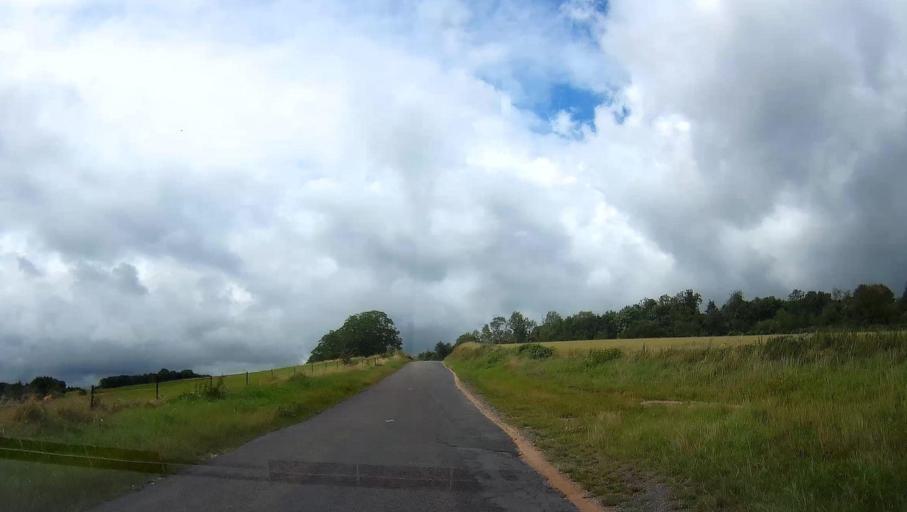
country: FR
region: Champagne-Ardenne
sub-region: Departement des Ardennes
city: Tournes
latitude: 49.7442
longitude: 4.5951
